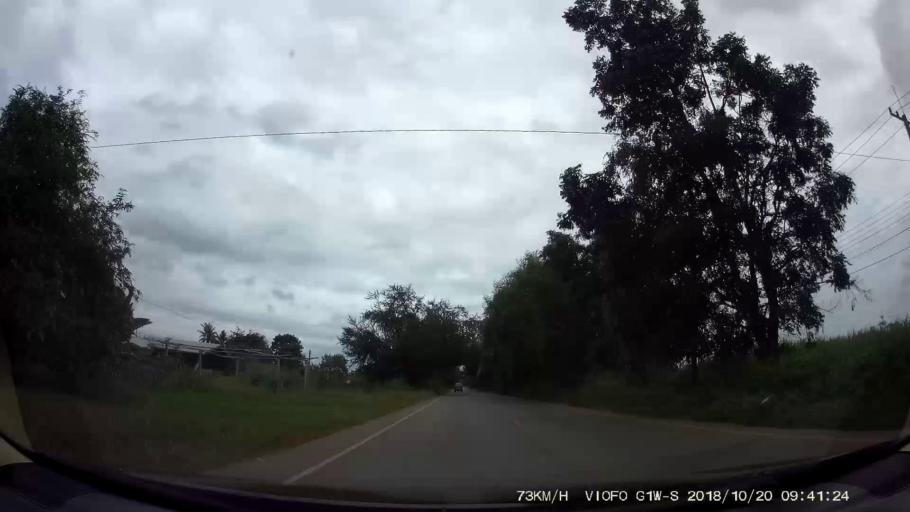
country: TH
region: Chaiyaphum
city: Khon San
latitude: 16.4530
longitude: 101.9571
